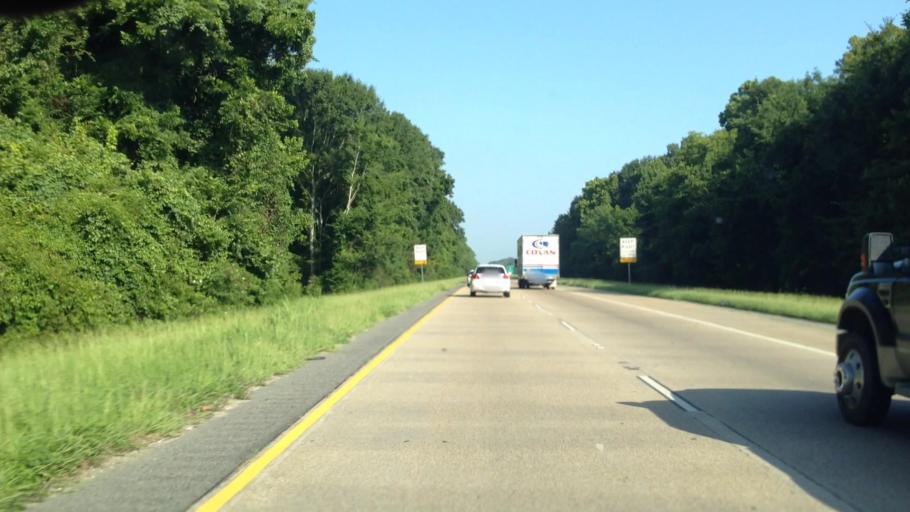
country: US
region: Louisiana
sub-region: Ascension Parish
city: Sorrento
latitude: 30.1790
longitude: -90.8920
